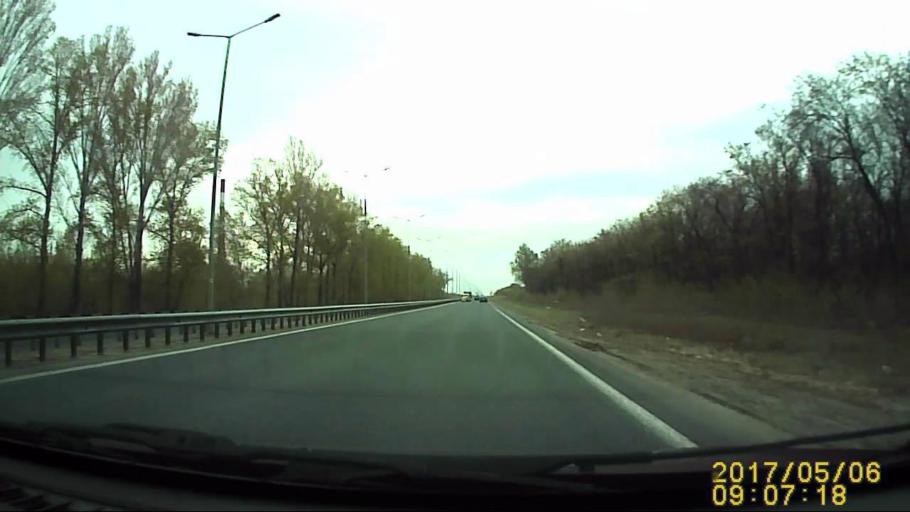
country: RU
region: Ulyanovsk
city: Mirnyy
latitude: 54.3411
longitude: 48.6045
